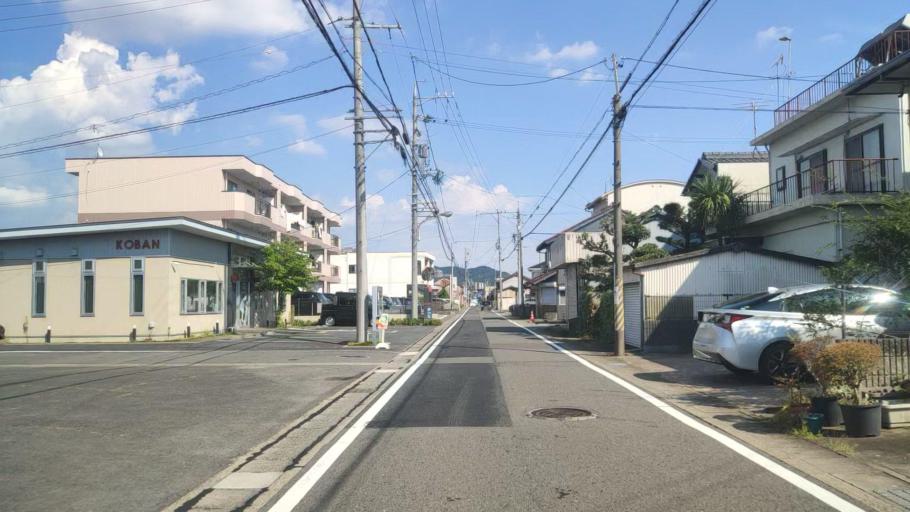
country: JP
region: Gifu
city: Gifu-shi
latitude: 35.4438
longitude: 136.7435
